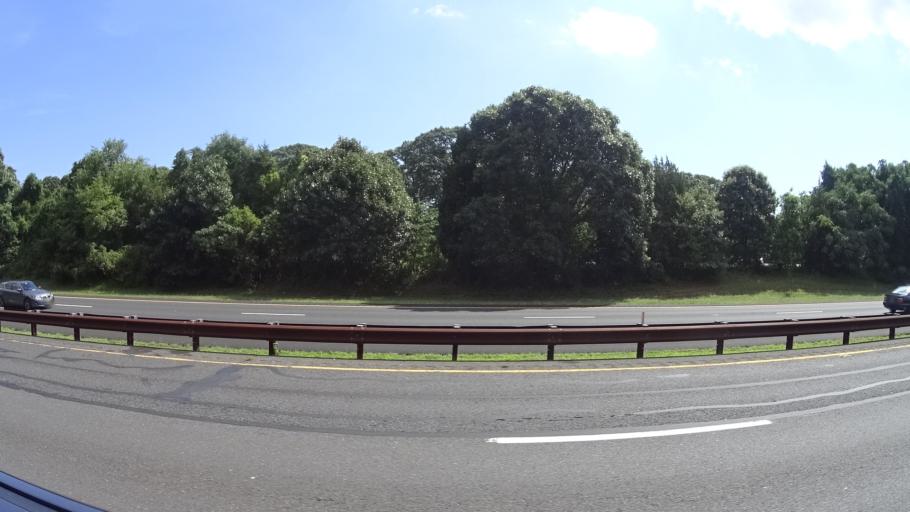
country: US
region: New Jersey
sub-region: Monmouth County
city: Lincroft
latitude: 40.3282
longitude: -74.0988
